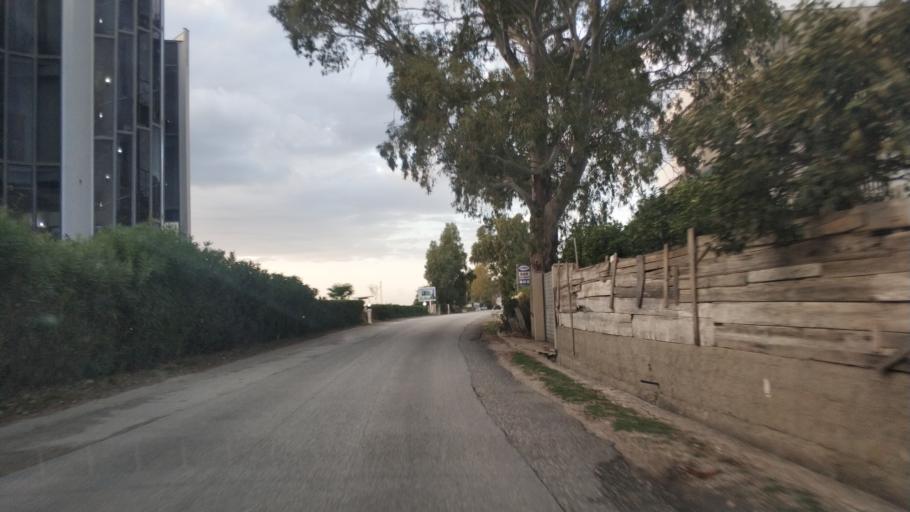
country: AL
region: Vlore
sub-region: Rrethi i Vlores
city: Orikum
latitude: 40.3552
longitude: 19.4837
